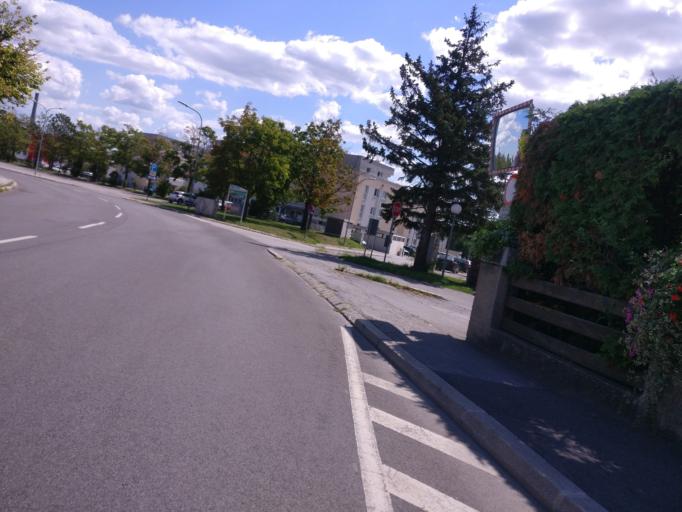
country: AT
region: Lower Austria
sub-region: Politischer Bezirk Neunkirchen
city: Neunkirchen
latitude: 47.7252
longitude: 16.0927
